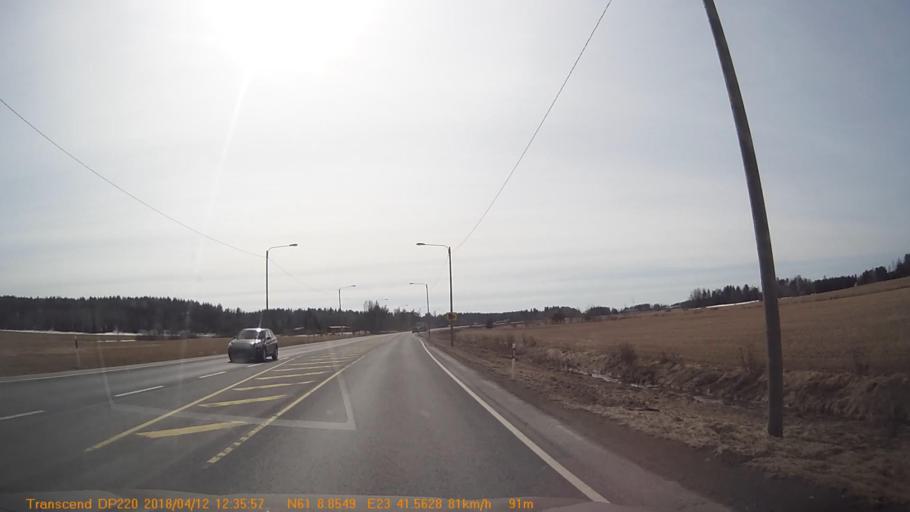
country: FI
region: Pirkanmaa
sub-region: Etelae-Pirkanmaa
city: Kylmaekoski
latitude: 61.1478
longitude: 23.6928
